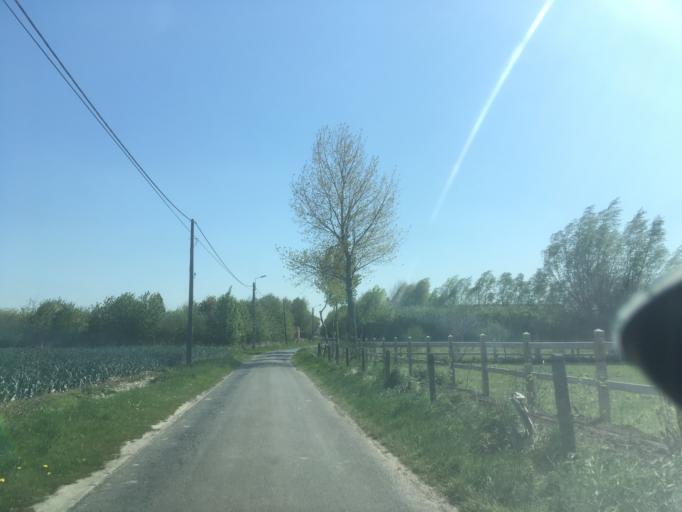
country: BE
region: Flanders
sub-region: Provincie West-Vlaanderen
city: Ardooie
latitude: 50.9600
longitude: 3.2186
